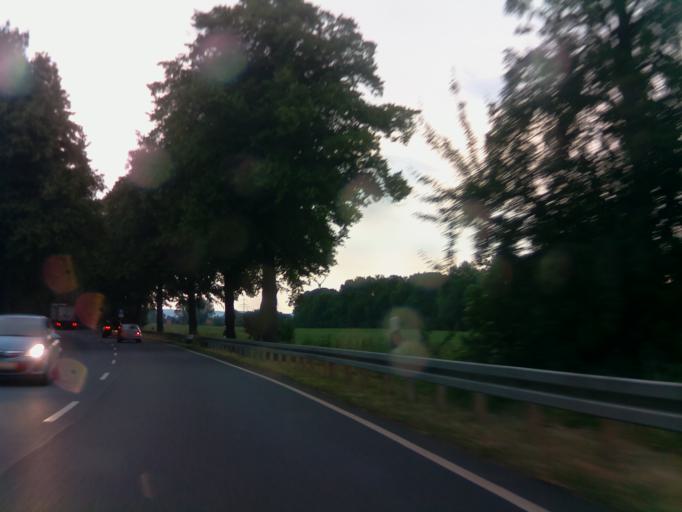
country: DE
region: Lower Saxony
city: Salzhemmendorf
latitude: 52.0840
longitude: 9.6097
